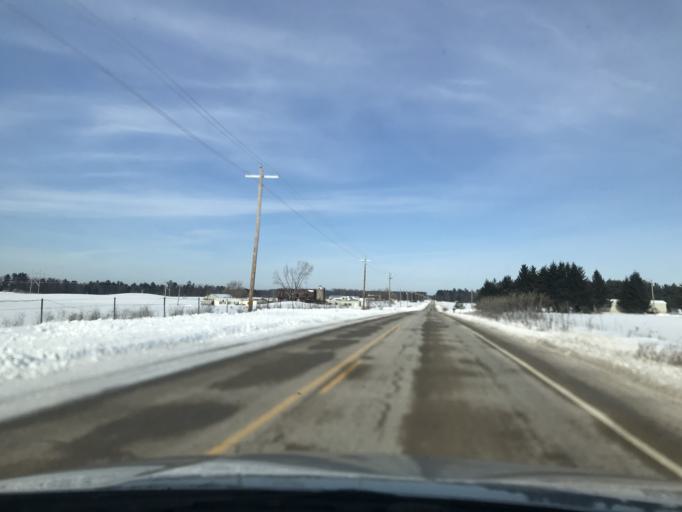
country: US
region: Wisconsin
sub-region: Oconto County
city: Oconto Falls
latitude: 45.1241
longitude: -88.1780
